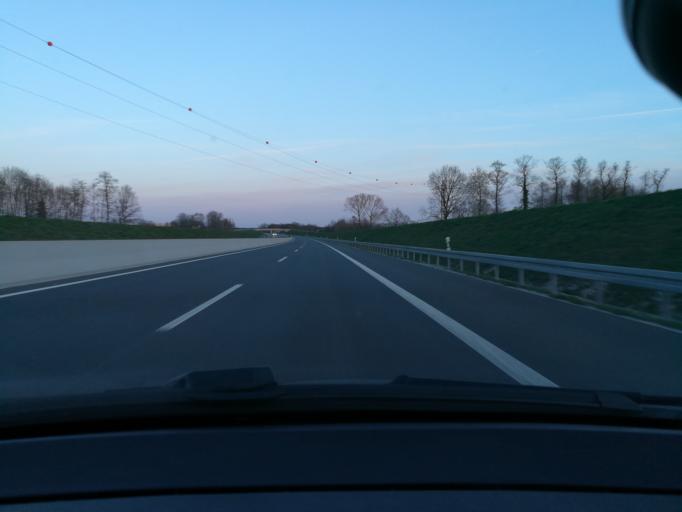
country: DE
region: North Rhine-Westphalia
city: Halle
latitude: 52.0331
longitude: 8.3511
